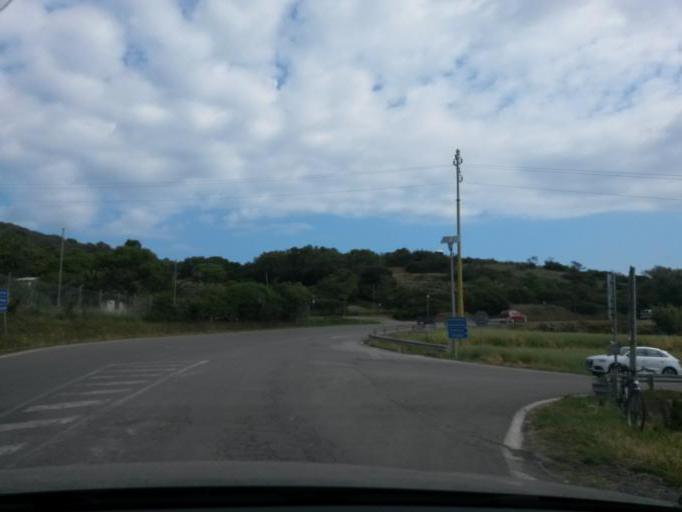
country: IT
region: Tuscany
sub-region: Provincia di Livorno
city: Portoferraio
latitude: 42.7927
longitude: 10.3356
